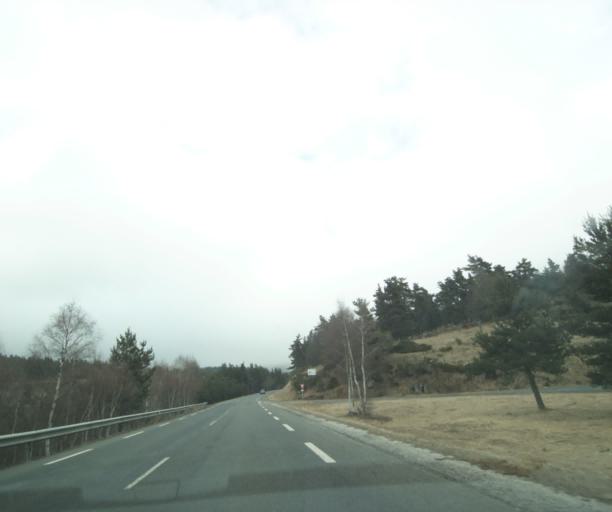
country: FR
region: Languedoc-Roussillon
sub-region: Departement de la Lozere
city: Langogne
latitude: 44.6575
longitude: 3.7454
